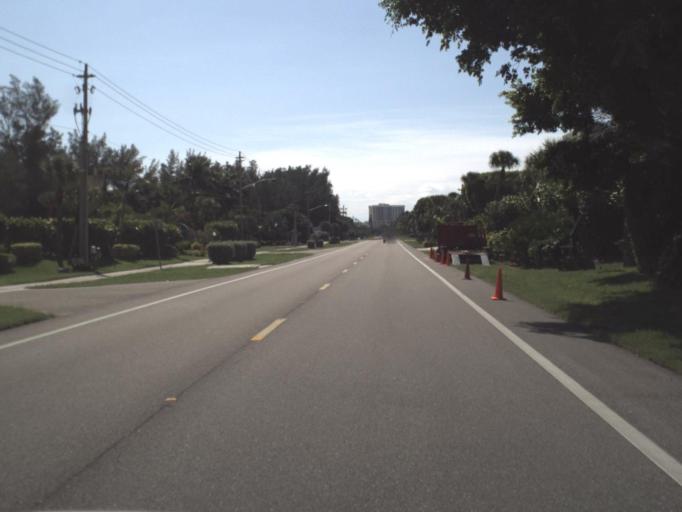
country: US
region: Florida
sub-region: Manatee County
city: Longboat Key
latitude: 27.3753
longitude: -82.6325
